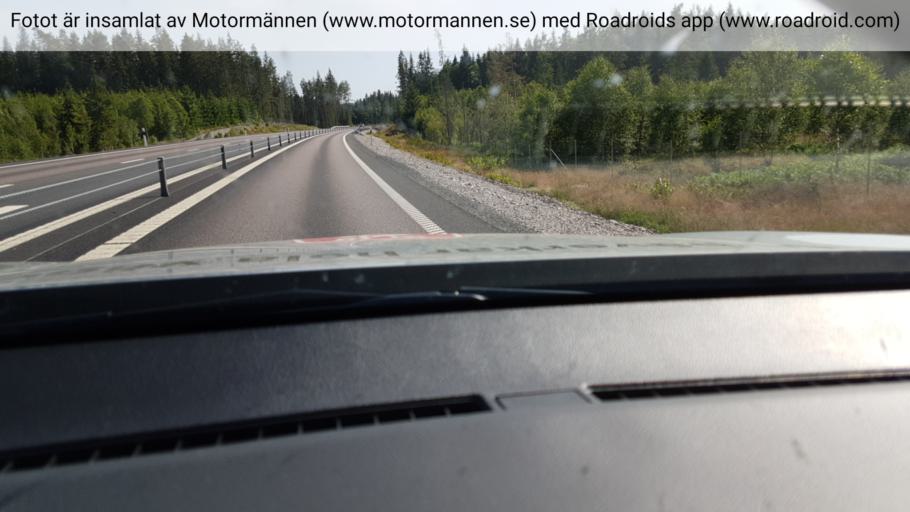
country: SE
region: Joenkoeping
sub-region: Aneby Kommun
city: Aneby
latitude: 57.8299
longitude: 14.8731
